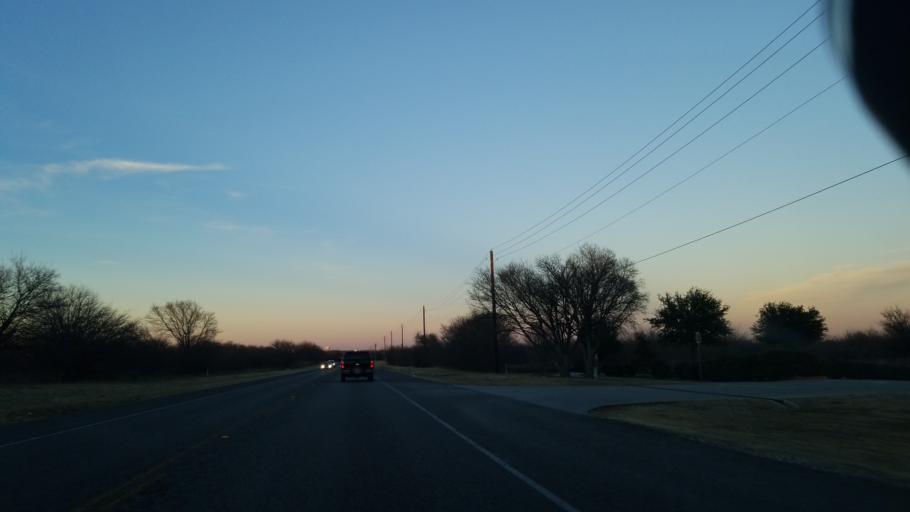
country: US
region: Texas
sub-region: Denton County
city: Argyle
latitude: 33.1404
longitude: -97.1739
